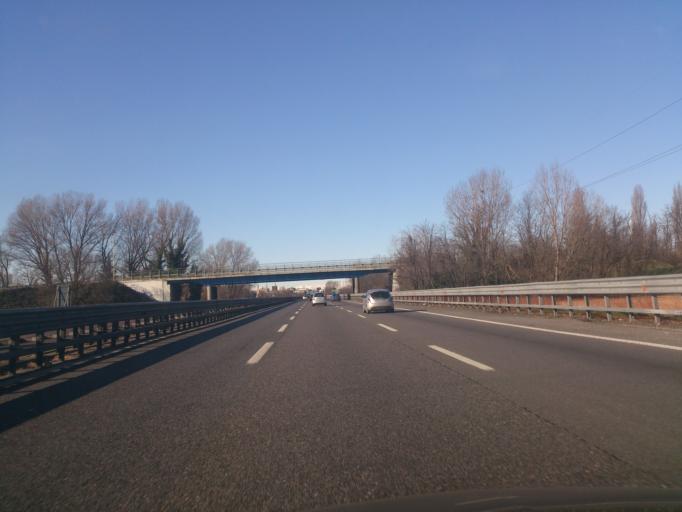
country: IT
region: Lombardy
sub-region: Citta metropolitana di Milano
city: Buccinasco
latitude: 45.4118
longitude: 9.1030
